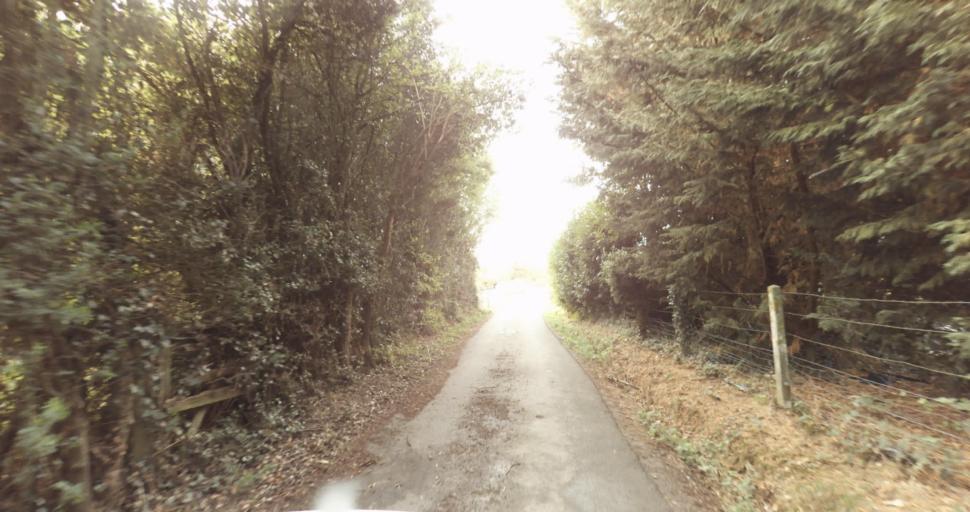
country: FR
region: Lower Normandy
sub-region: Departement de l'Orne
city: Vimoutiers
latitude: 48.9126
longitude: 0.3048
